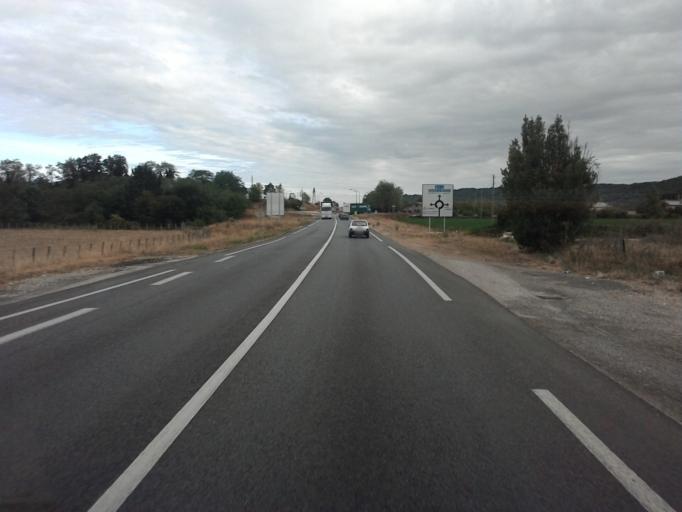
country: FR
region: Rhone-Alpes
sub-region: Departement de l'Ain
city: Vaux-en-Bugey
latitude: 45.9236
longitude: 5.3400
